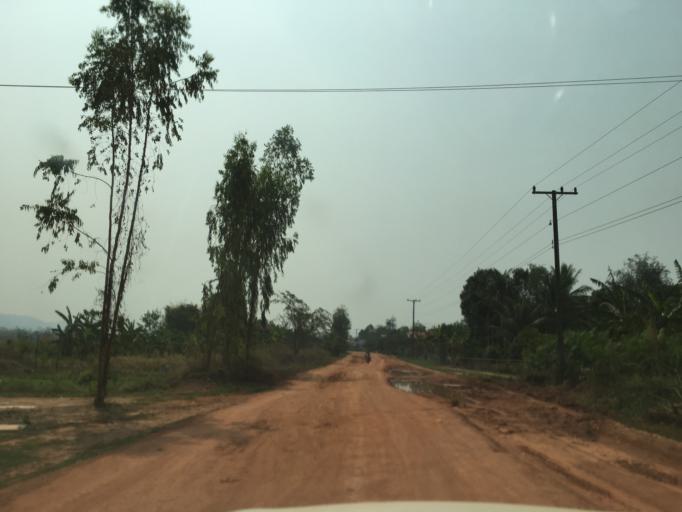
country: TH
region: Changwat Bueng Kan
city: Bung Khla
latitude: 18.2288
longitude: 104.0637
